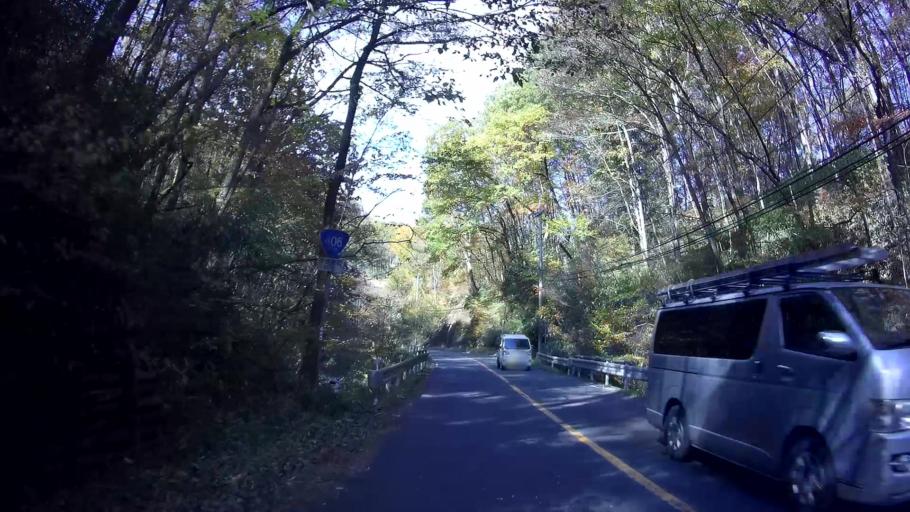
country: JP
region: Gunma
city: Nakanojomachi
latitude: 36.4917
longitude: 138.7758
